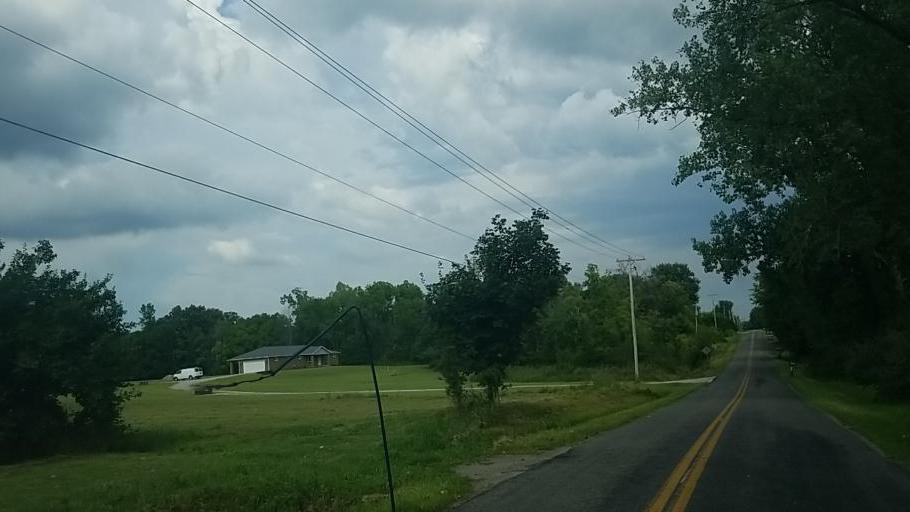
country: US
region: Ohio
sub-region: Wayne County
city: Creston
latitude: 40.9953
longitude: -81.9094
